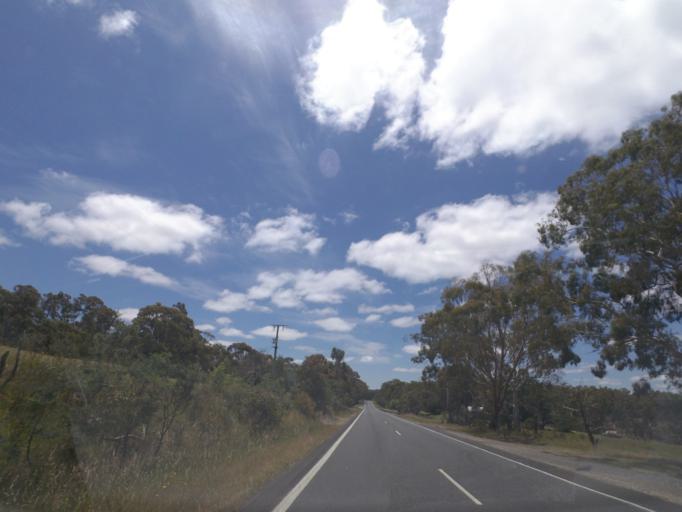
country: AU
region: Victoria
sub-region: Mount Alexander
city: Castlemaine
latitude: -37.2963
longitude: 144.1626
